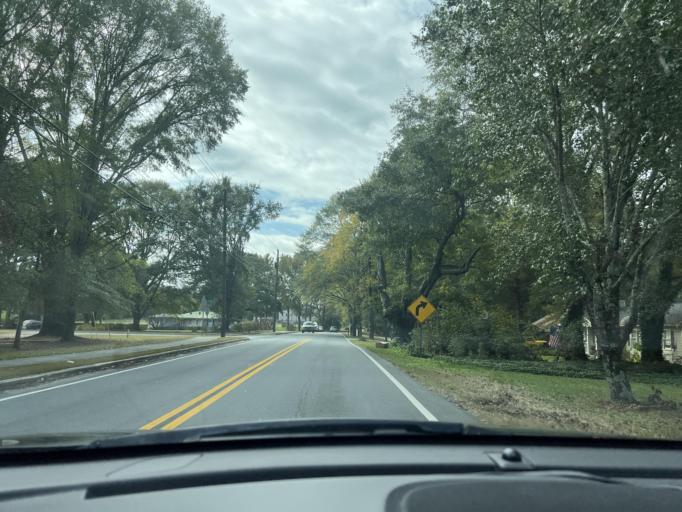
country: US
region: Georgia
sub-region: Gwinnett County
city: Grayson
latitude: 33.8972
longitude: -83.9520
